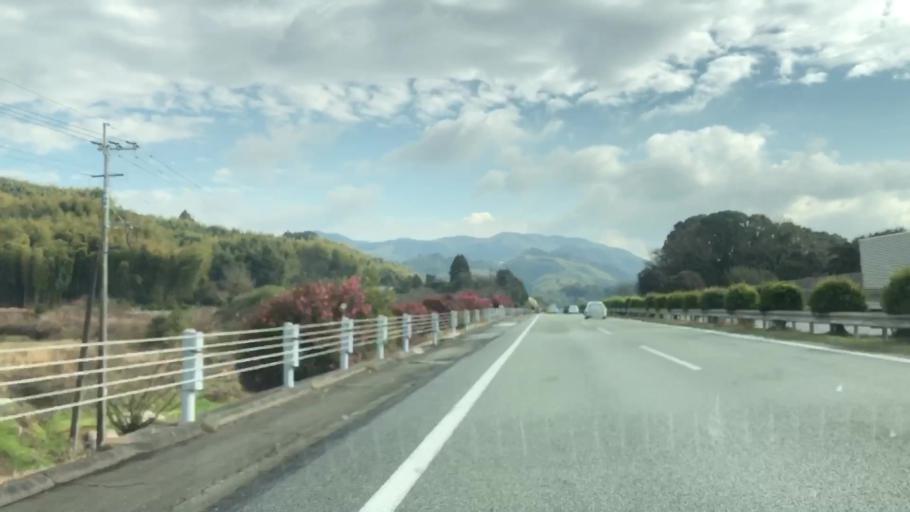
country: JP
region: Fukuoka
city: Setakamachi-takayanagi
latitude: 33.1188
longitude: 130.5241
